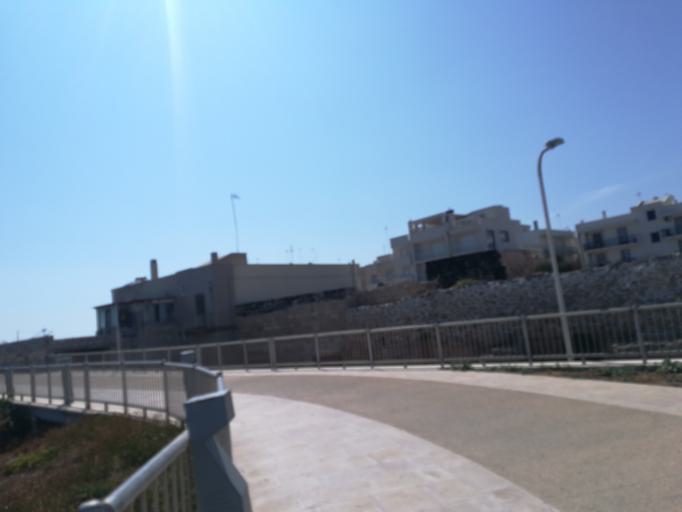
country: IT
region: Apulia
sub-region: Provincia di Bari
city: Polignano a Mare
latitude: 40.9960
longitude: 17.2260
